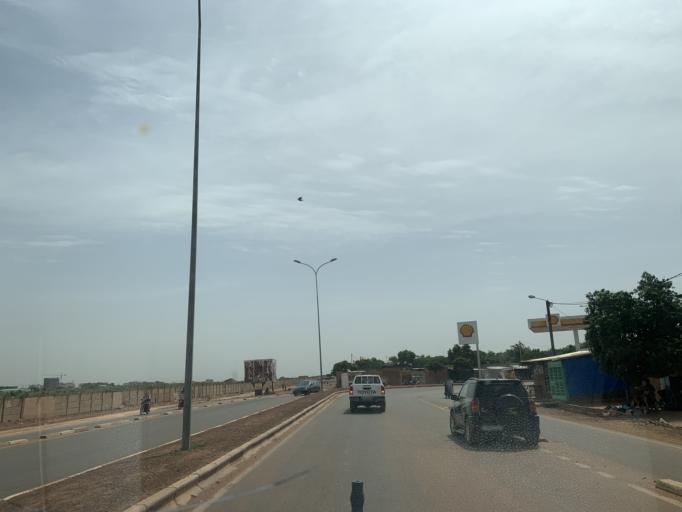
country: BF
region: Centre
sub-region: Kadiogo Province
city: Ouagadougou
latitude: 12.3390
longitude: -1.5180
